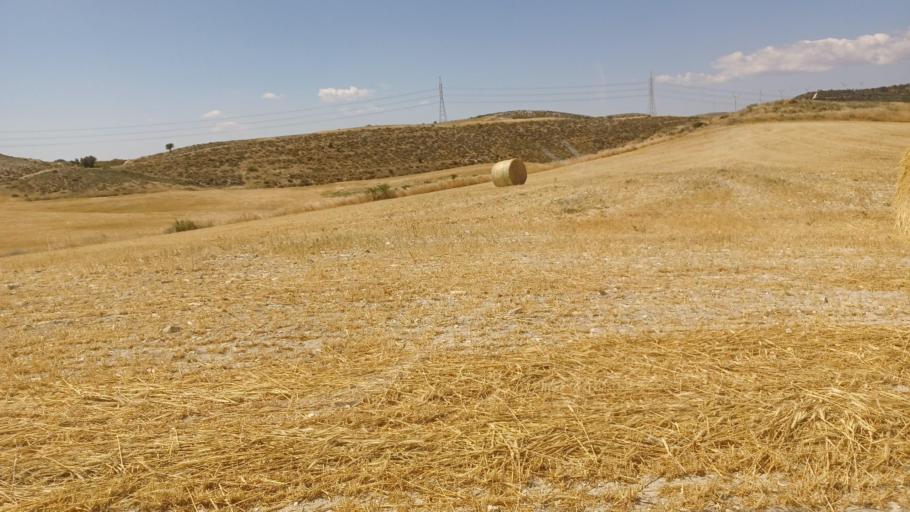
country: CY
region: Larnaka
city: Athienou
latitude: 34.9968
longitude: 33.5385
